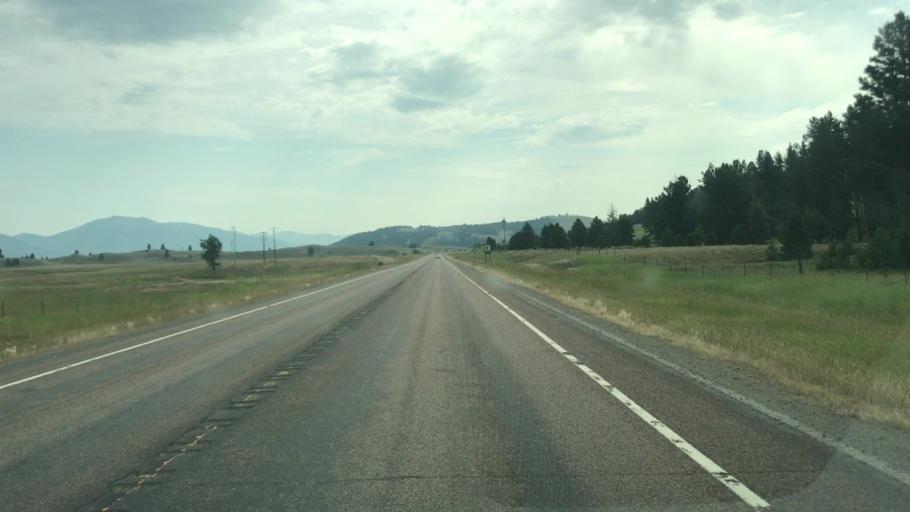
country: US
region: Montana
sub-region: Missoula County
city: Seeley Lake
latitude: 47.0304
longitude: -113.2681
